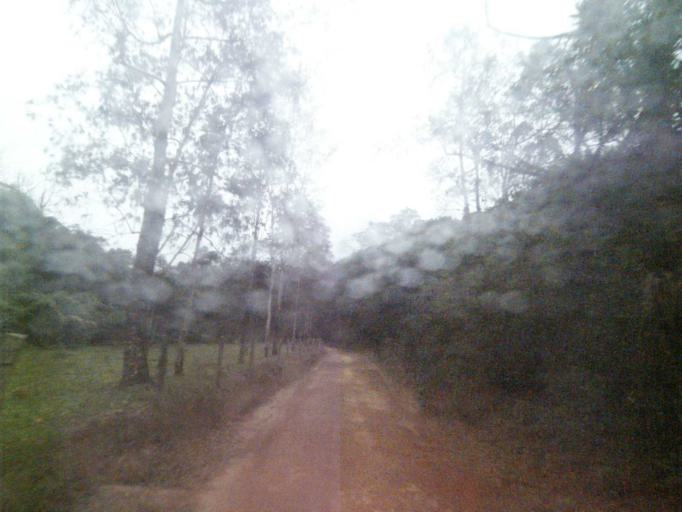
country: BR
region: Santa Catarina
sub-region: Anitapolis
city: Anitapolis
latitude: -27.8715
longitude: -49.1310
